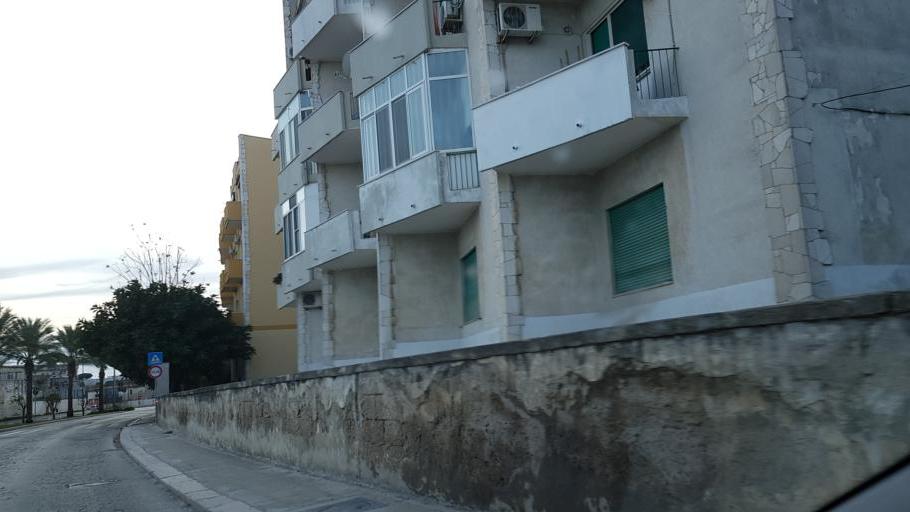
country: IT
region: Apulia
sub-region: Provincia di Brindisi
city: Brindisi
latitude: 40.6328
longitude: 17.9472
